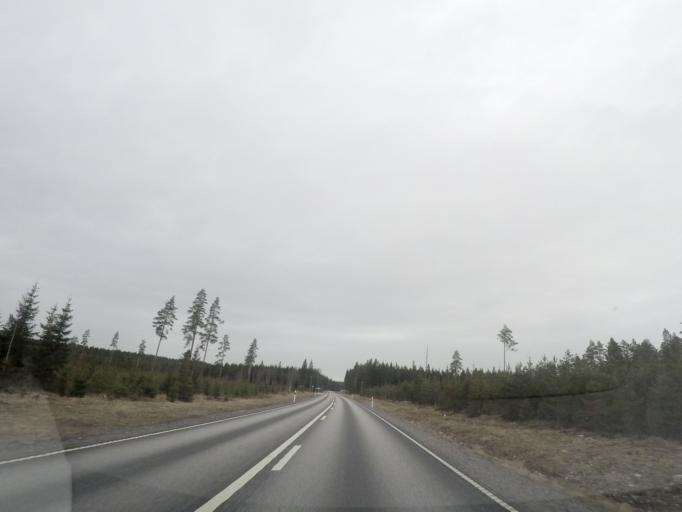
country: SE
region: OErebro
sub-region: Ljusnarsbergs Kommun
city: Kopparberg
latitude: 59.9635
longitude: 15.0208
